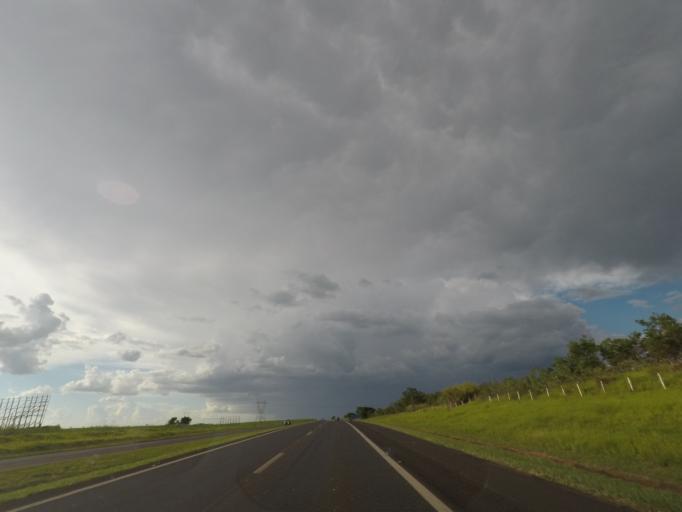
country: BR
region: Sao Paulo
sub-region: Jardinopolis
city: Jardinopolis
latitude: -21.0246
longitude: -47.8381
